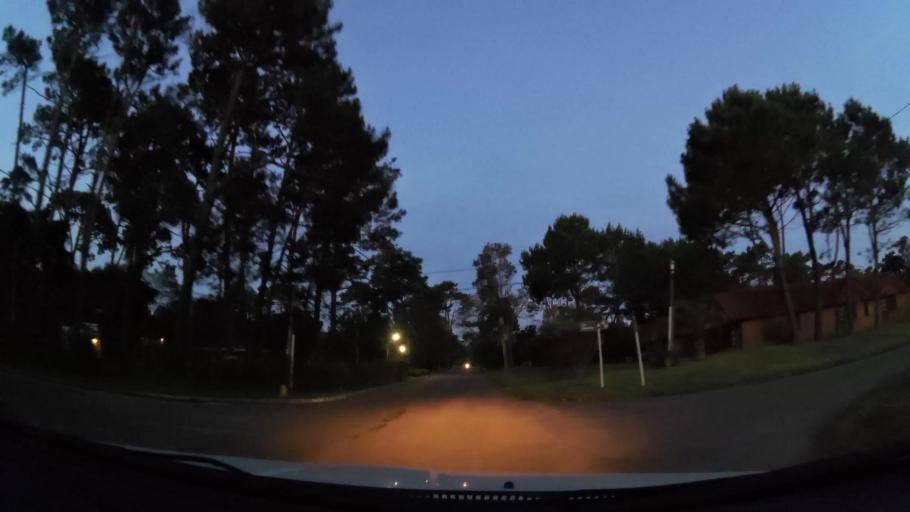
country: UY
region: Maldonado
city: Punta del Este
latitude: -34.9406
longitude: -54.9221
